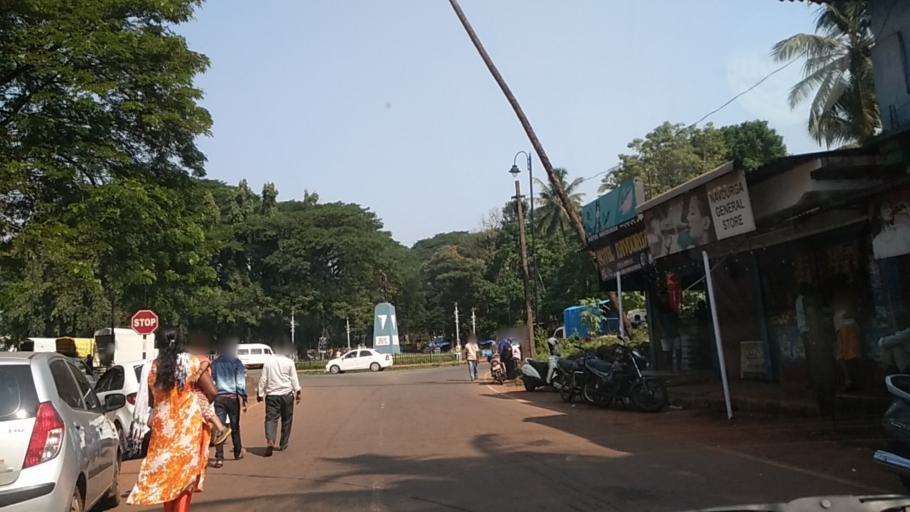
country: IN
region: Goa
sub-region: North Goa
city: Jua
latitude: 15.5008
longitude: 73.9136
